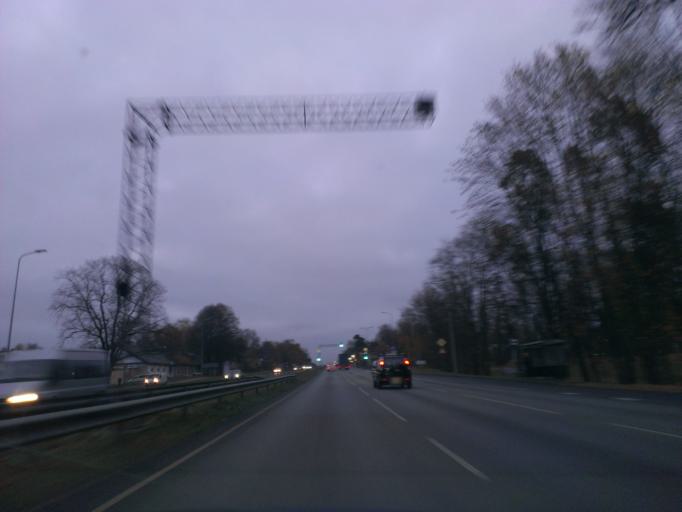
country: LV
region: Riga
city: Bergi
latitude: 56.9961
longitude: 24.2639
